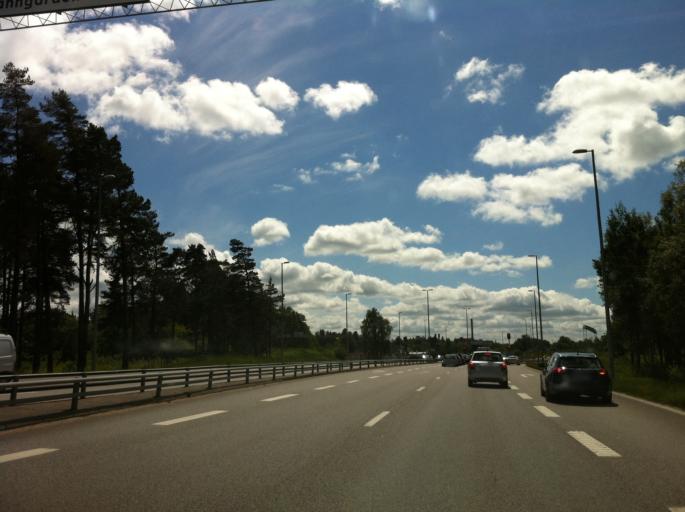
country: SE
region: Vaestra Goetaland
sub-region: Trollhattan
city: Trollhattan
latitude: 58.2642
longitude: 12.2925
